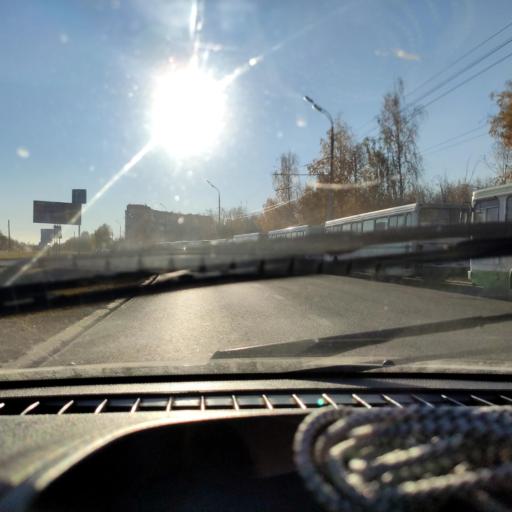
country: RU
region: Samara
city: Tol'yatti
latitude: 53.5051
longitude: 49.2554
